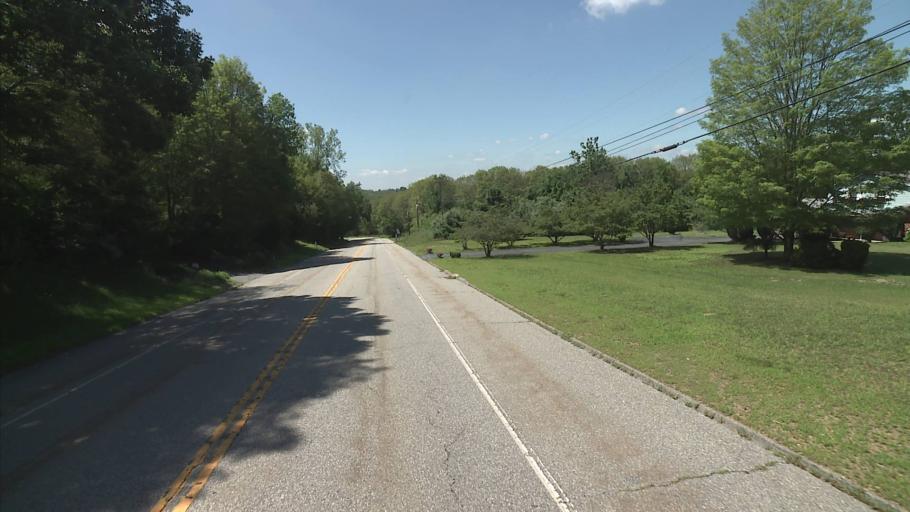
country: US
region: Connecticut
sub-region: Windham County
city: Plainfield Village
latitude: 41.7025
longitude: -71.9580
